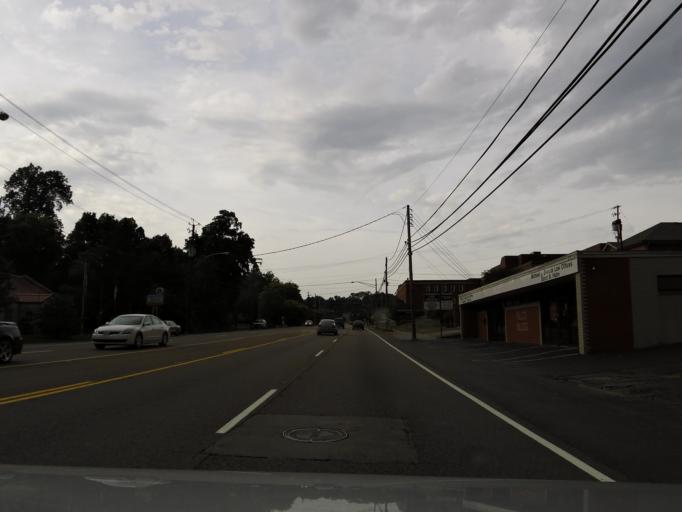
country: US
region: Tennessee
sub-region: Knox County
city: Knoxville
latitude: 36.0370
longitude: -83.9317
